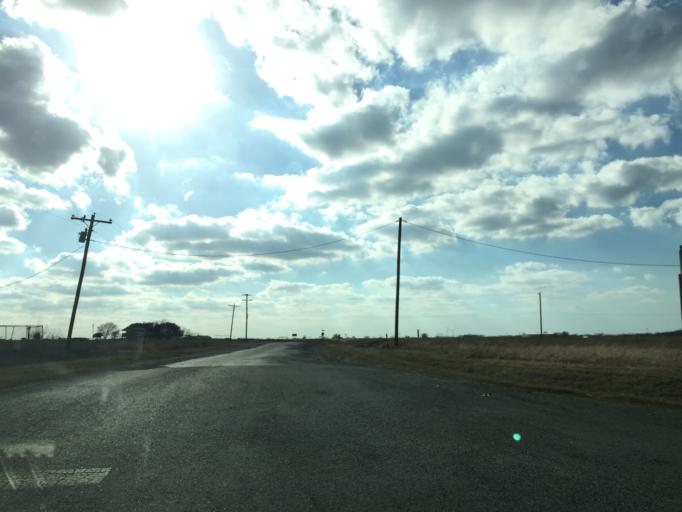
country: US
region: Texas
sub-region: Williamson County
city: Taylor
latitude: 30.6354
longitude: -97.4346
